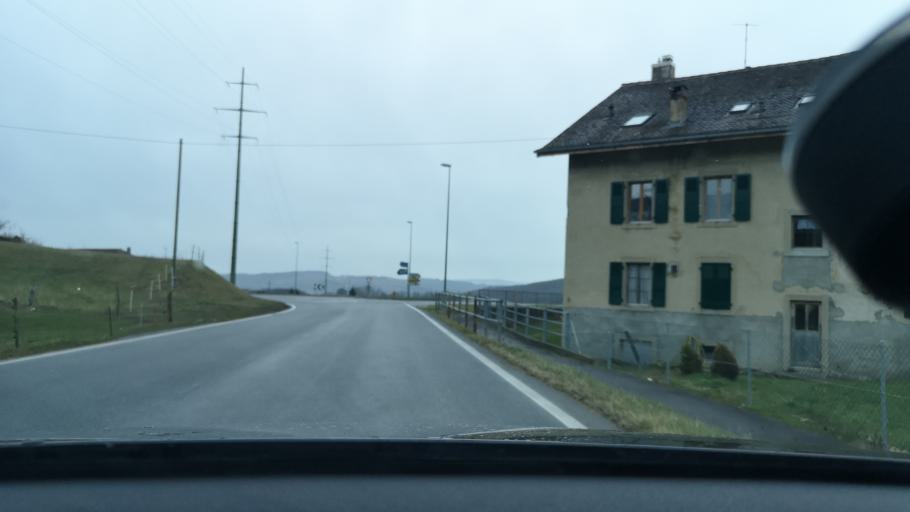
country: CH
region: Vaud
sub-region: Jura-Nord vaudois District
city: Montagny
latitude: 46.7924
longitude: 6.5805
